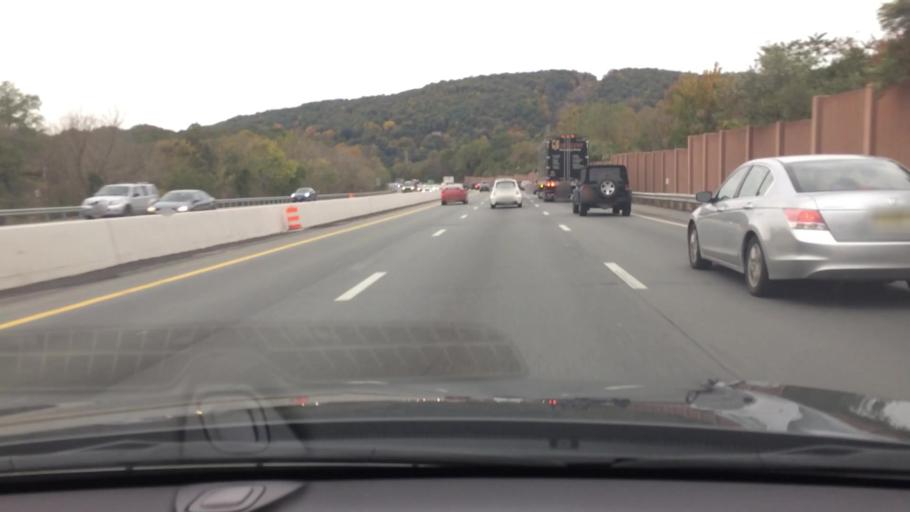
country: US
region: New York
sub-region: Rockland County
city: Suffern
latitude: 41.1210
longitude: -74.1326
